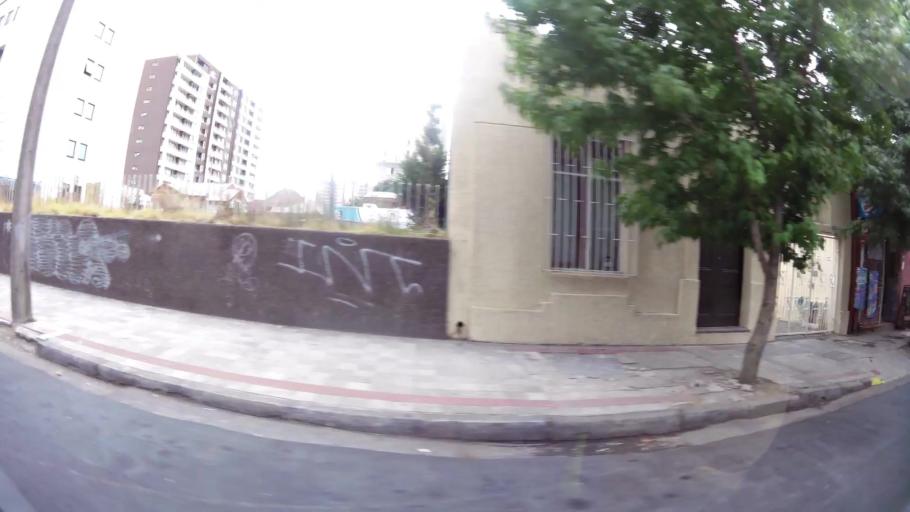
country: CL
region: Biobio
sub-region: Provincia de Concepcion
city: Concepcion
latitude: -36.8212
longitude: -73.0409
